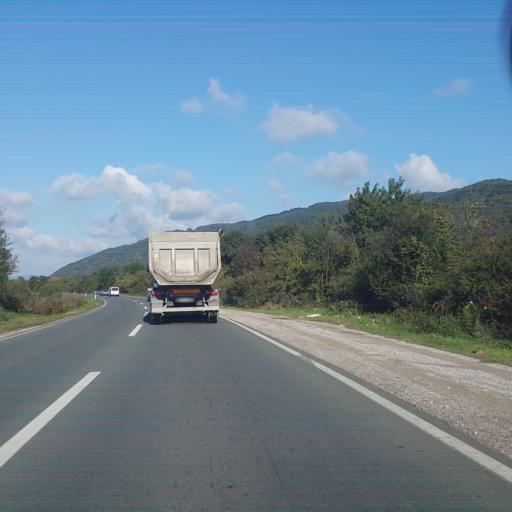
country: RS
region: Central Serbia
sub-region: Rasinski Okrug
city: Trstenik
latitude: 43.6281
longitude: 20.9721
